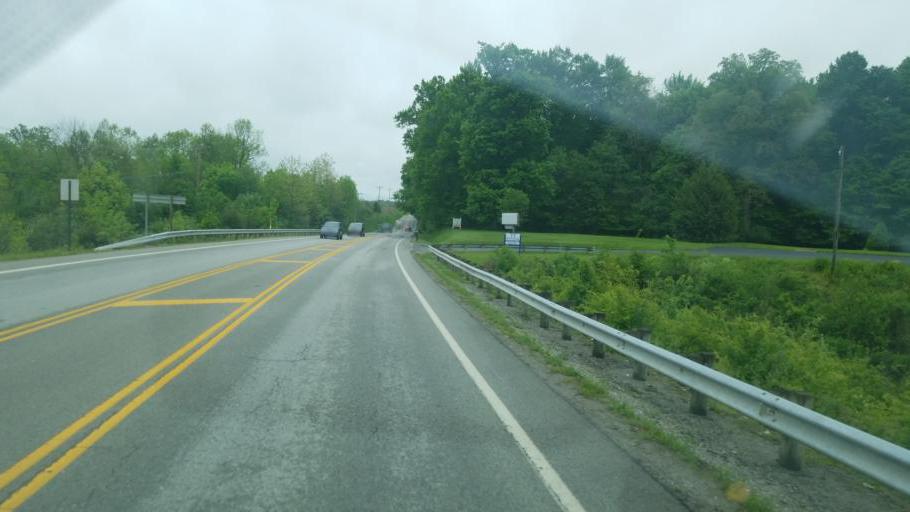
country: US
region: Ohio
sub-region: Highland County
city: Hillsboro
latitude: 39.2240
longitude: -83.6237
